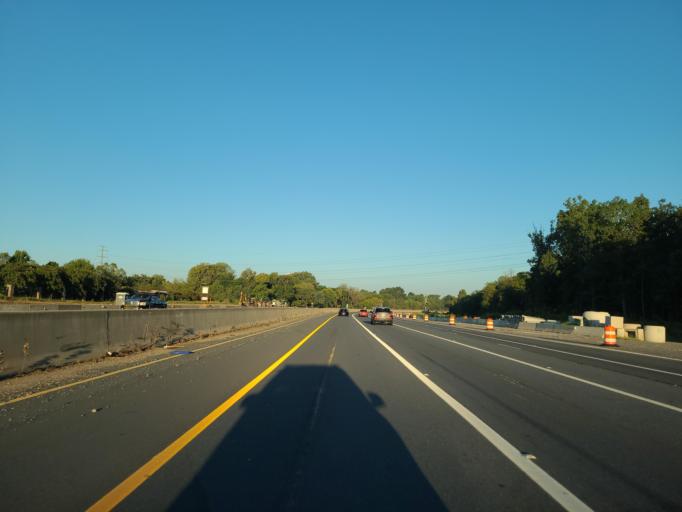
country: US
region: North Carolina
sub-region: Mecklenburg County
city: Pineville
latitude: 35.0653
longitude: -80.8545
